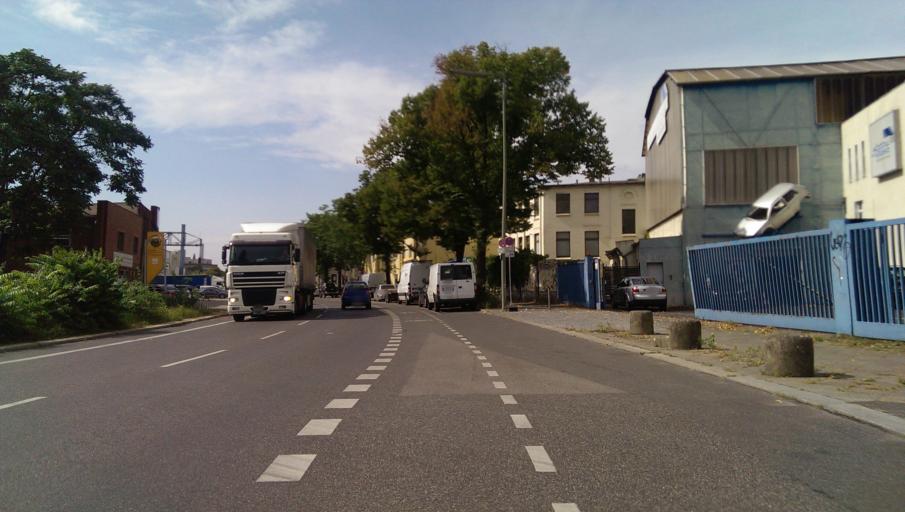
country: DE
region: Berlin
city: Tempelhof Bezirk
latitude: 52.4601
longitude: 13.4061
